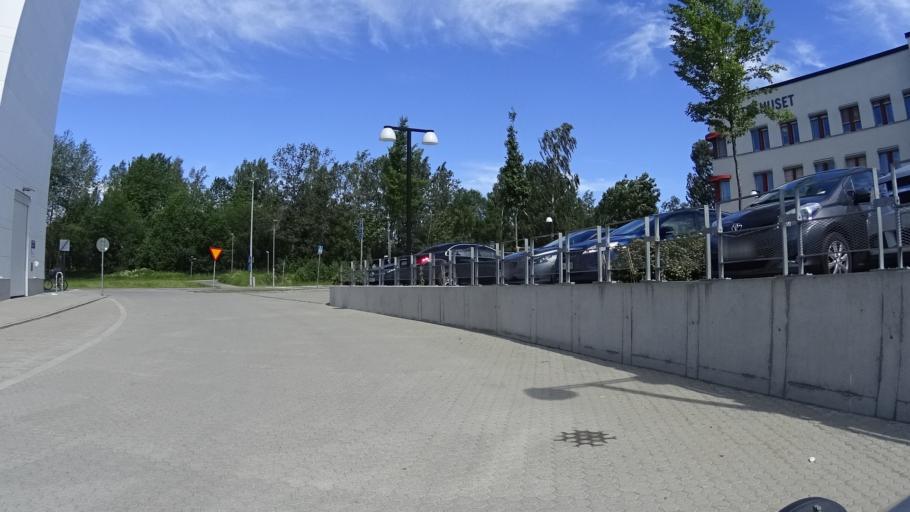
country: SE
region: OErebro
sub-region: Orebro Kommun
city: Orebro
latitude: 59.2546
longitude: 15.2449
